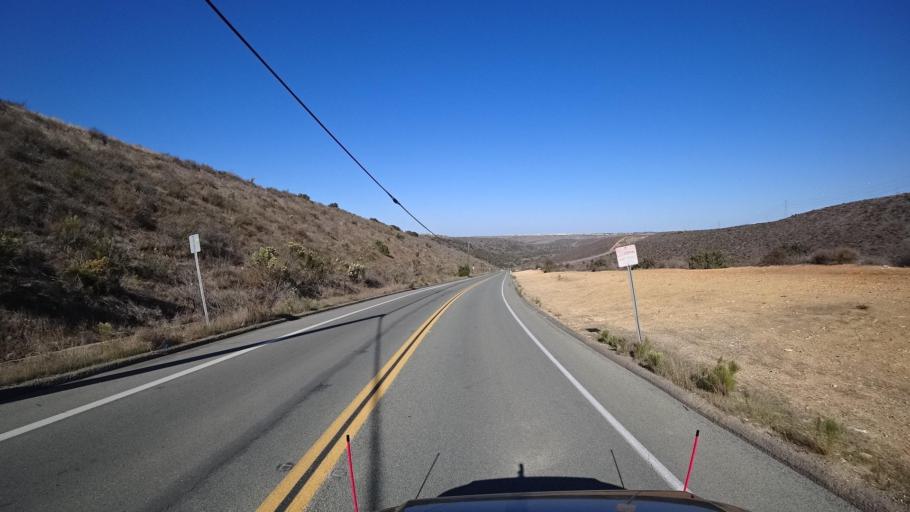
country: MX
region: Baja California
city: Tijuana
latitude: 32.5837
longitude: -116.9226
